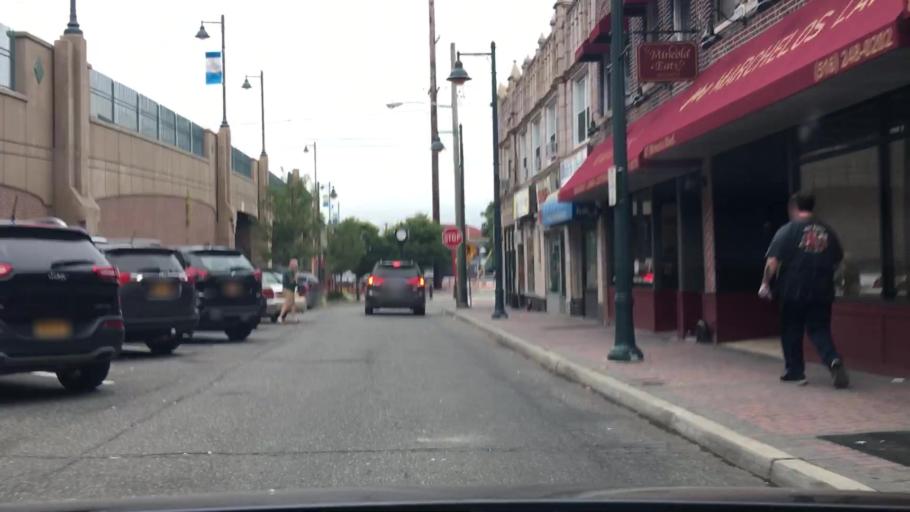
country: US
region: New York
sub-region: Nassau County
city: Mineola
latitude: 40.7413
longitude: -73.6404
